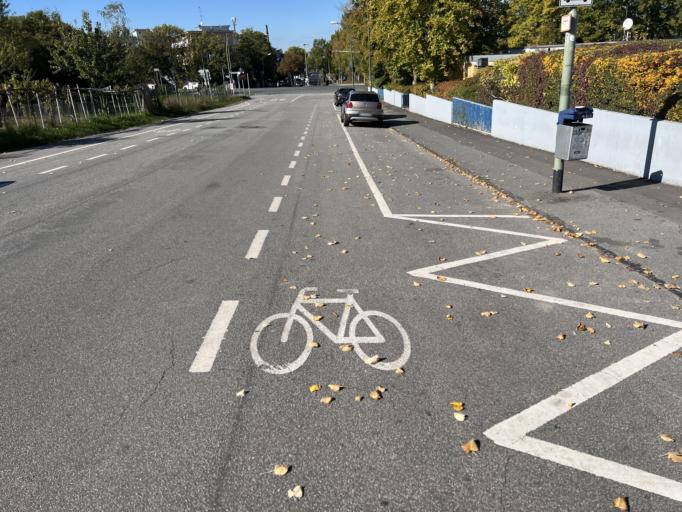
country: DE
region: Hesse
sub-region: Regierungsbezirk Darmstadt
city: Offenbach
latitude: 50.0917
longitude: 8.7809
